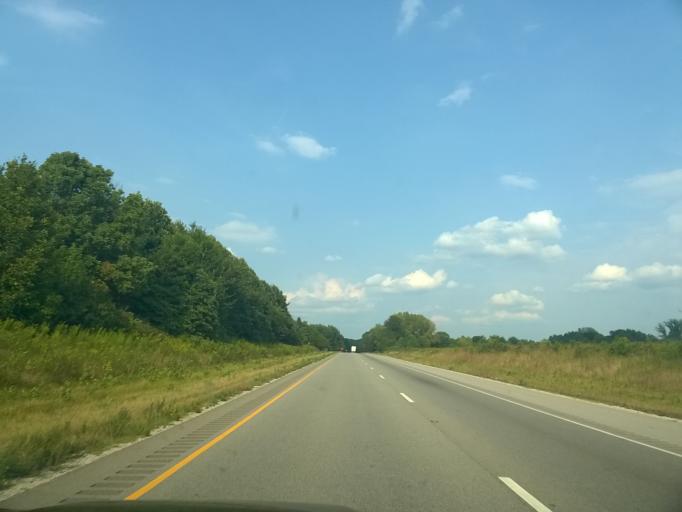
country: US
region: Indiana
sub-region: Vigo County
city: Seelyville
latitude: 39.4393
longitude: -87.2799
